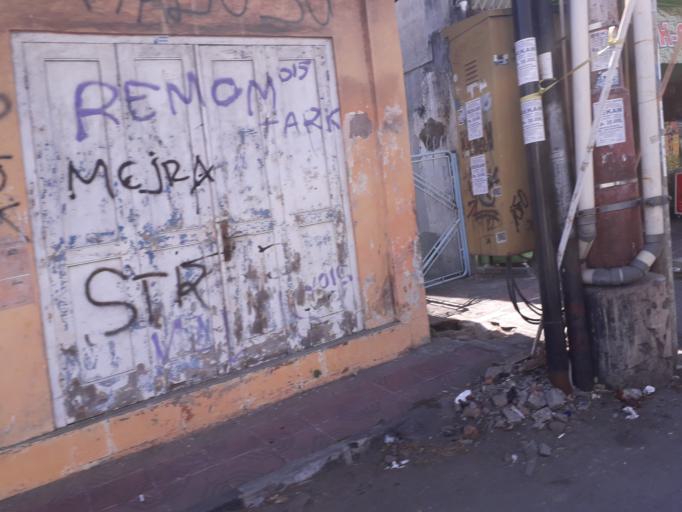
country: ID
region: Daerah Istimewa Yogyakarta
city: Yogyakarta
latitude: -7.7955
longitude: 110.3691
